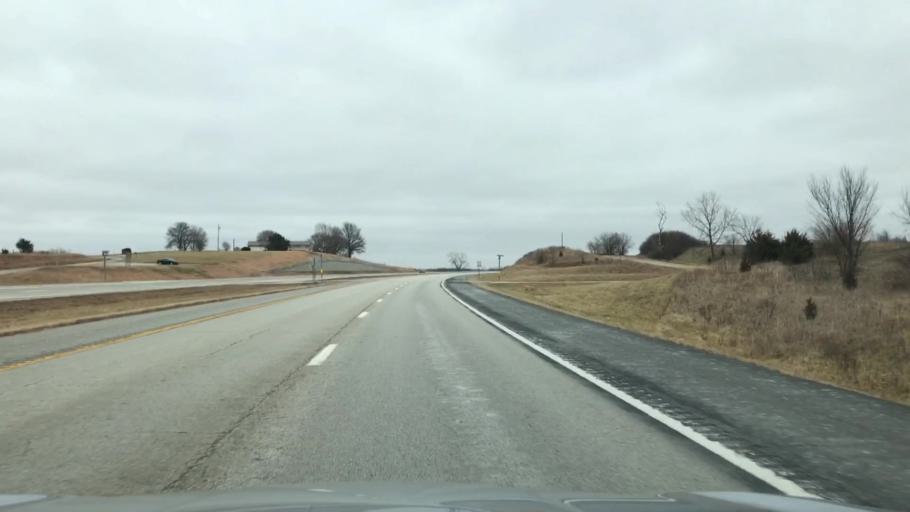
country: US
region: Missouri
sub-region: Caldwell County
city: Hamilton
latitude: 39.7488
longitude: -94.0571
